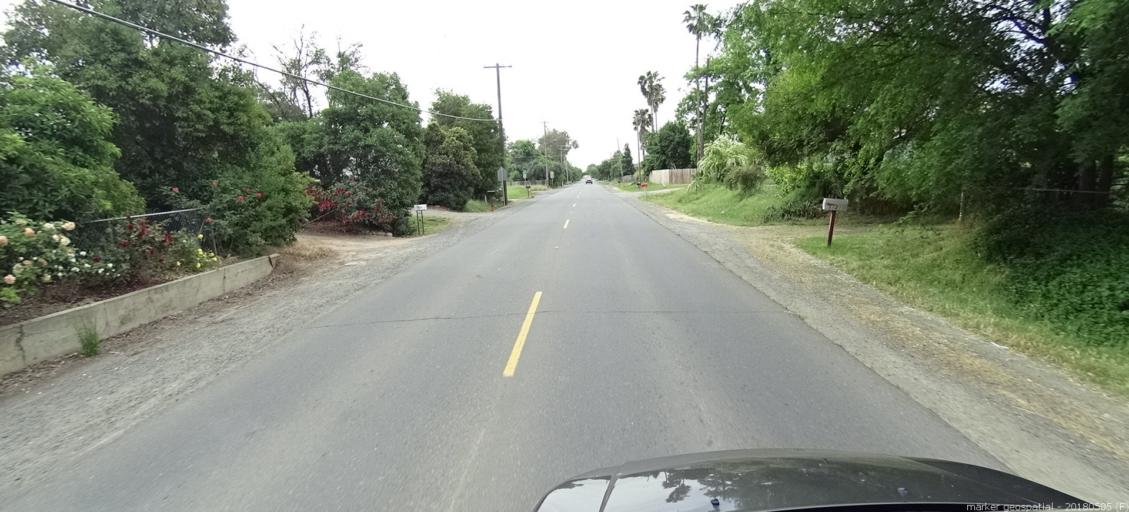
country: US
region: California
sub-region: Sacramento County
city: Rio Linda
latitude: 38.6609
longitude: -121.4462
